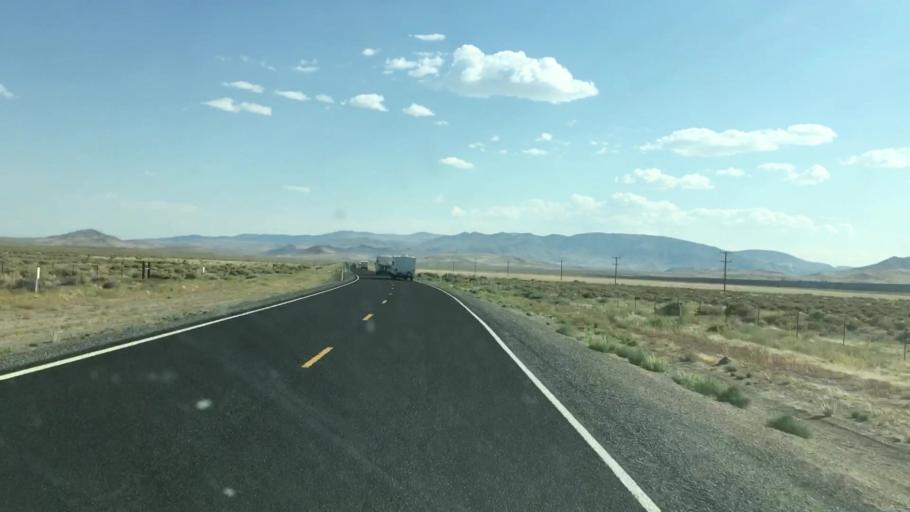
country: US
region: Nevada
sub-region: Lyon County
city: Fernley
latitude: 39.6856
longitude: -119.3352
